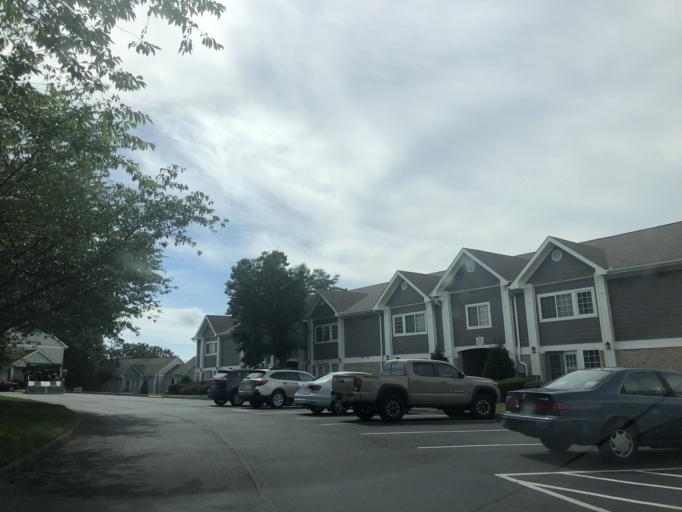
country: US
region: Tennessee
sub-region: Davidson County
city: Belle Meade
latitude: 36.0737
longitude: -86.9419
